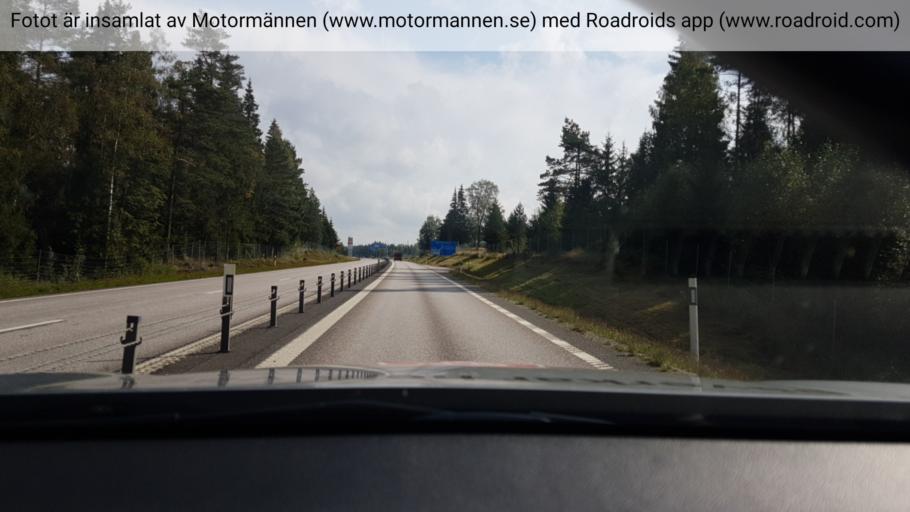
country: SE
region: Vaestra Goetaland
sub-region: Ulricehamns Kommun
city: Ulricehamn
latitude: 57.7810
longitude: 13.6557
